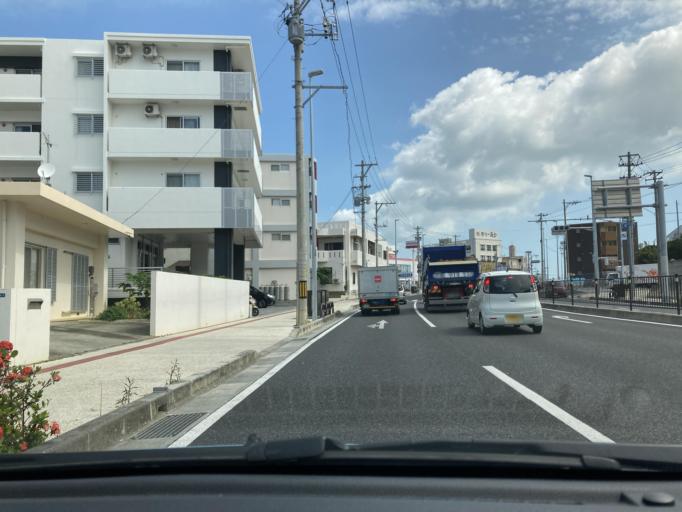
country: JP
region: Okinawa
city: Ginowan
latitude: 26.2572
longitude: 127.7549
